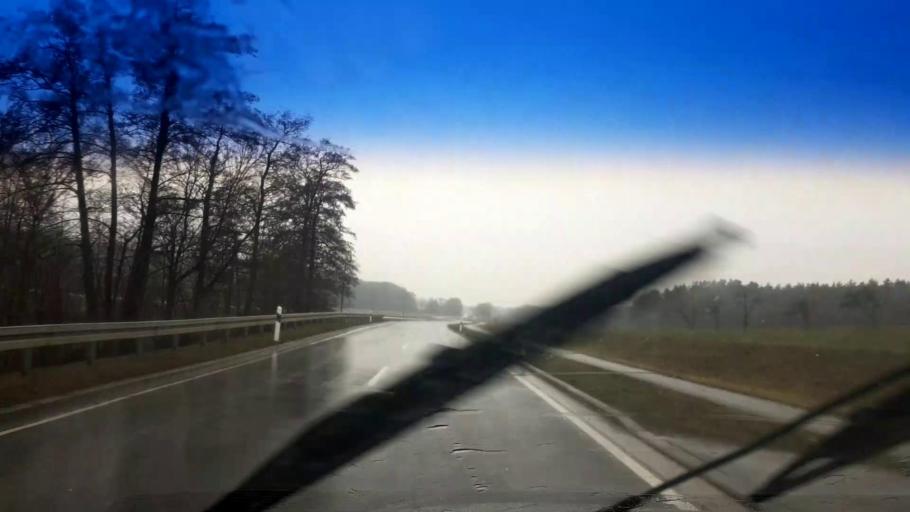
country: DE
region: Bavaria
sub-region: Upper Franconia
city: Litzendorf
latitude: 49.9149
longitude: 10.9855
